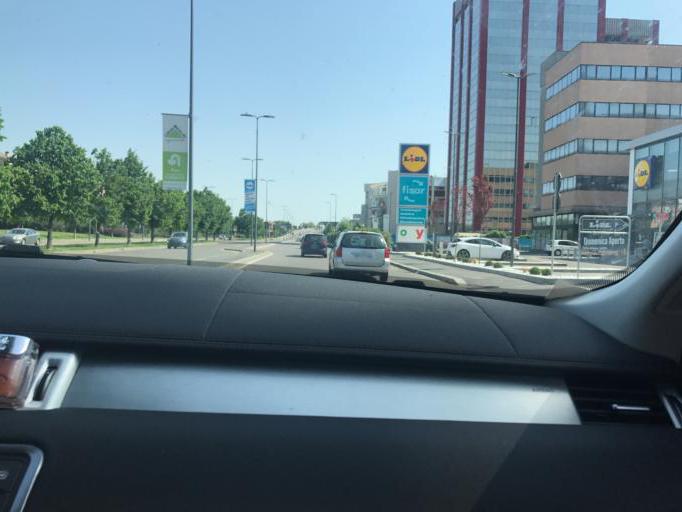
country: IT
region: Lombardy
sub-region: Citta metropolitana di Milano
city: Romano Banco
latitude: 45.4450
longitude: 9.1220
